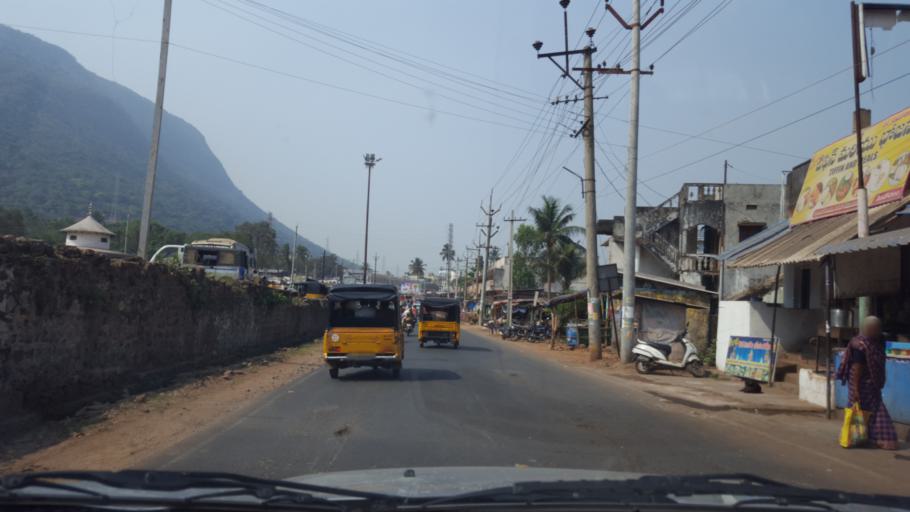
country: IN
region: Andhra Pradesh
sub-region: Vishakhapatnam
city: Vepagunta
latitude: 17.7736
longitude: 83.2459
